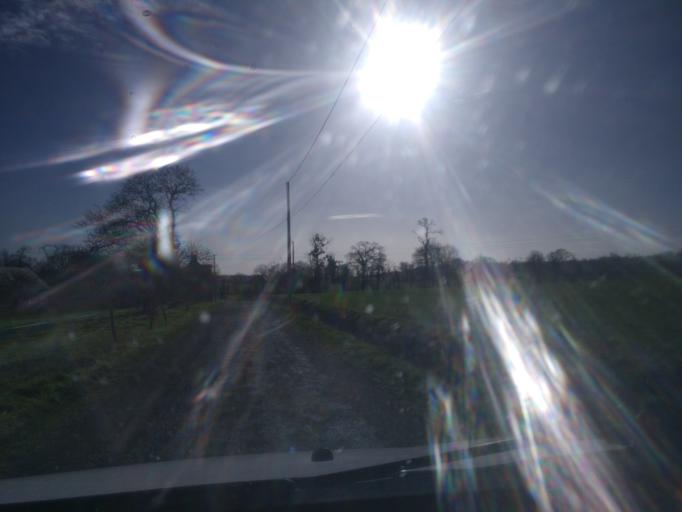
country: FR
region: Lower Normandy
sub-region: Departement de la Manche
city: Pontorson
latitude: 48.5195
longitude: -1.5195
